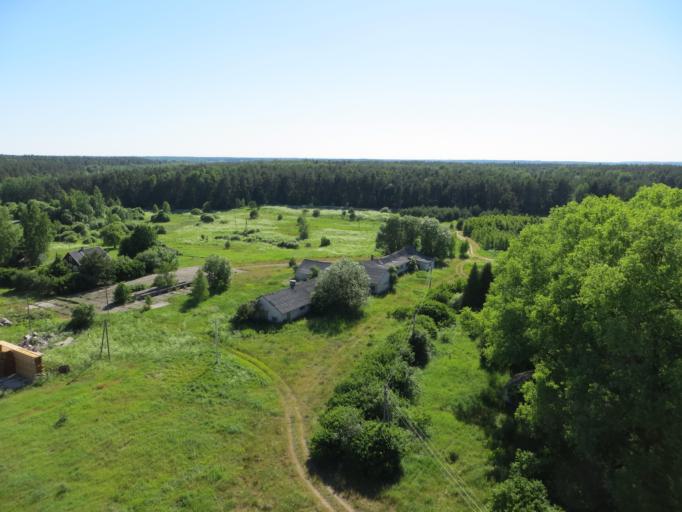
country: LT
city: Moletai
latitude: 55.0752
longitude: 25.2468
